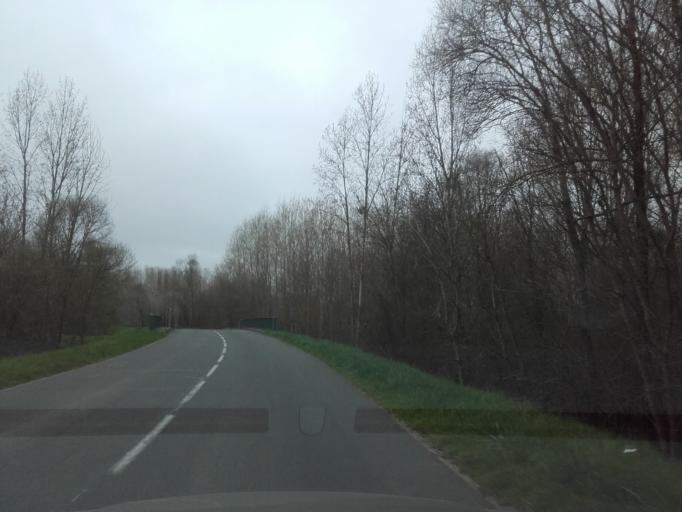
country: FR
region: Centre
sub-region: Departement d'Indre-et-Loire
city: Cheille
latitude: 47.2744
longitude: 0.3698
